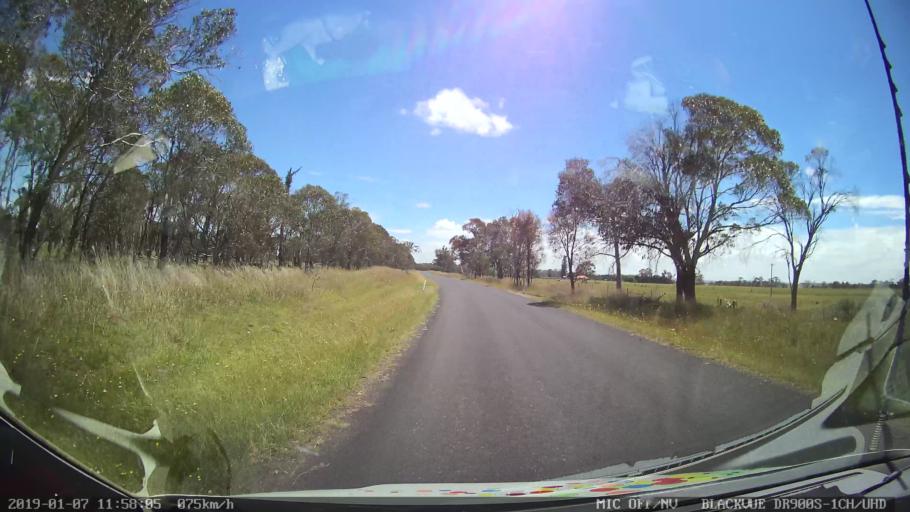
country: AU
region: New South Wales
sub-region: Guyra
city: Guyra
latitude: -30.2574
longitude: 151.6673
